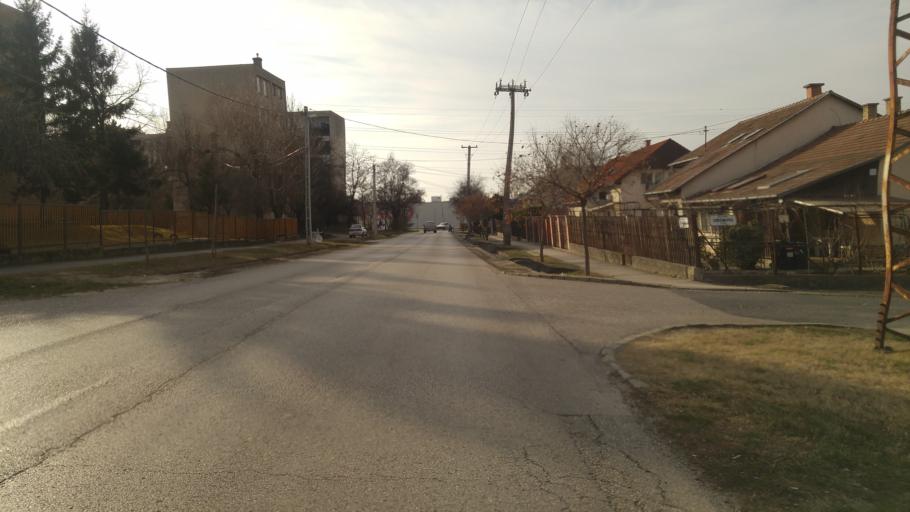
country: HU
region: Budapest
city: Budapest XVII. keruelet
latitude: 47.4822
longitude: 19.2314
